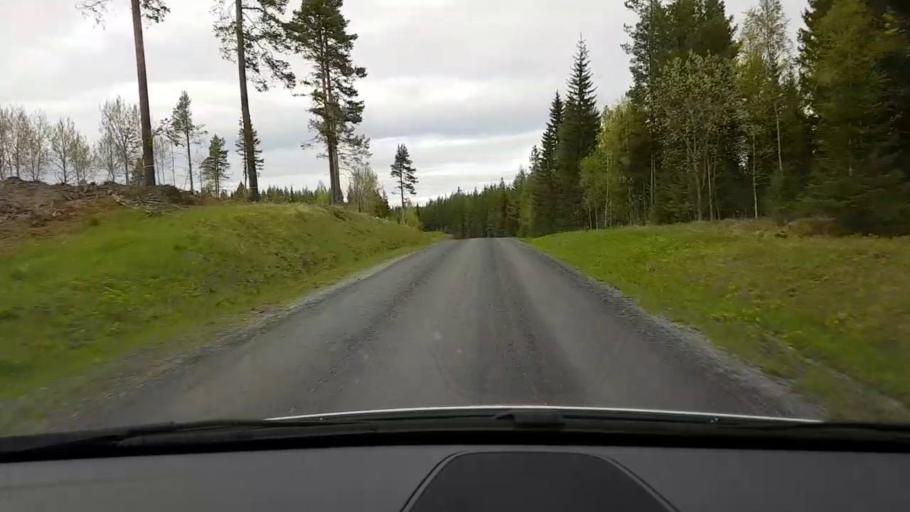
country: SE
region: Jaemtland
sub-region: Krokoms Kommun
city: Krokom
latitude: 63.3009
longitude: 14.3975
